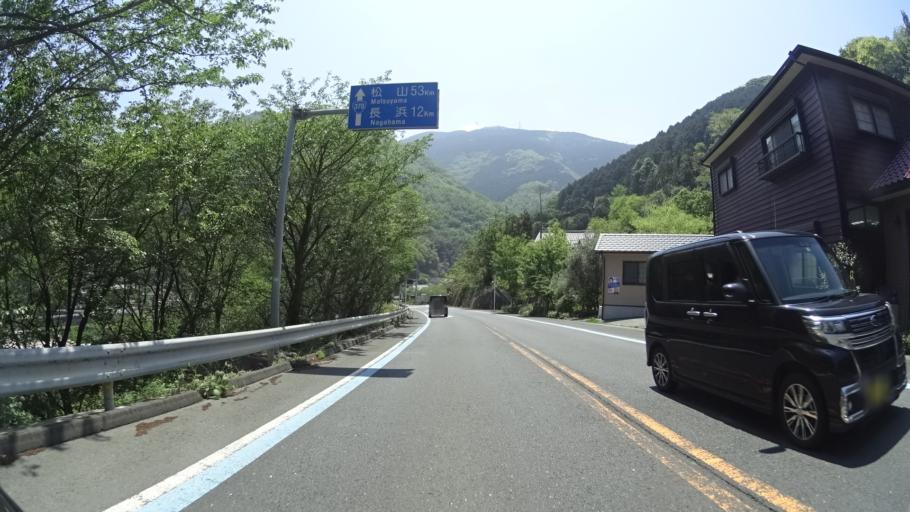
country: JP
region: Ehime
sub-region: Nishiuwa-gun
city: Ikata-cho
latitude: 33.5379
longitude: 132.4051
